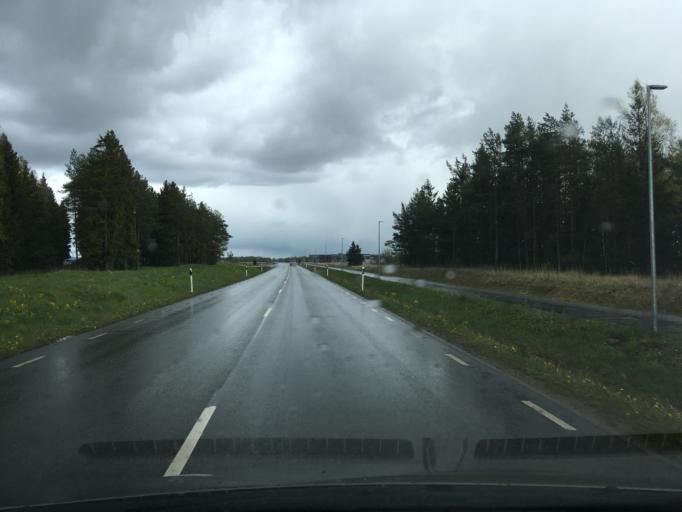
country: EE
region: Harju
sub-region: Joelaehtme vald
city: Loo
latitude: 59.4464
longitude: 24.9469
